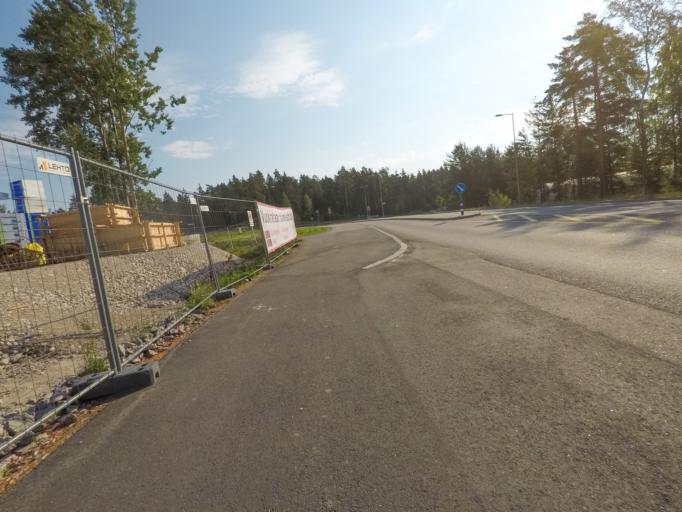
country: FI
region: Uusimaa
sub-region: Helsinki
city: Vantaa
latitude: 60.3001
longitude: 24.9639
